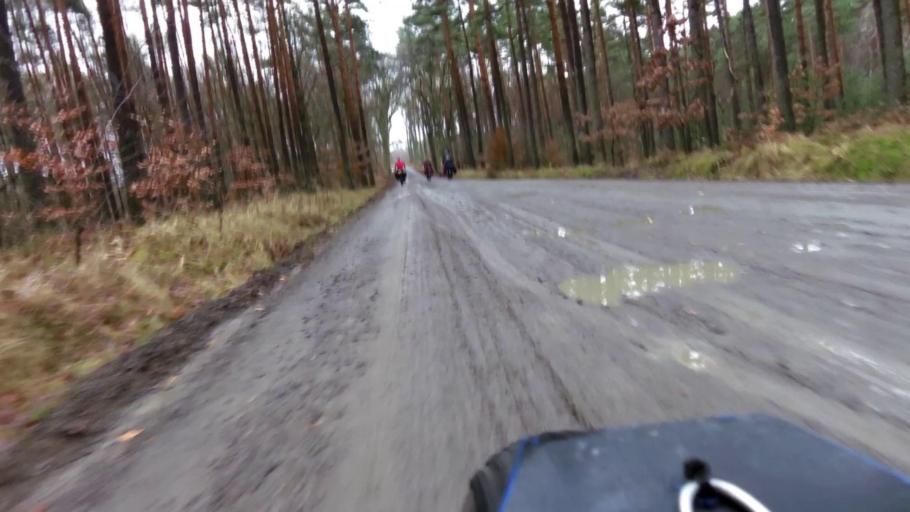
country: PL
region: Lubusz
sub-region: Powiat gorzowski
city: Witnica
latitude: 52.7040
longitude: 14.8308
